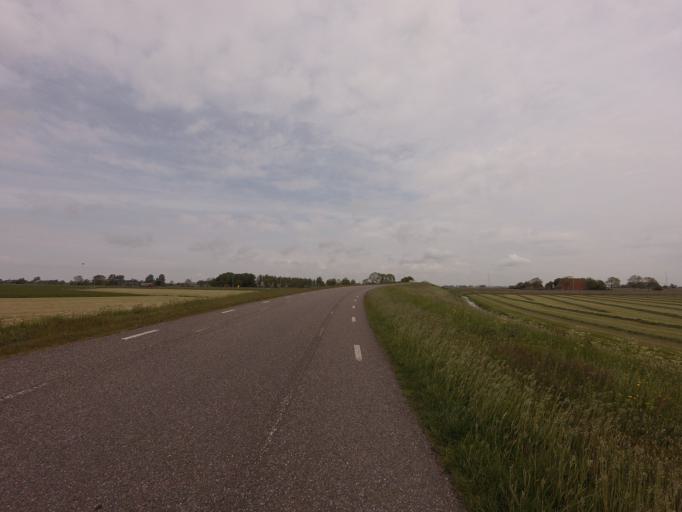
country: NL
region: Friesland
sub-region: Sudwest Fryslan
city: Bolsward
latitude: 53.0742
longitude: 5.4776
